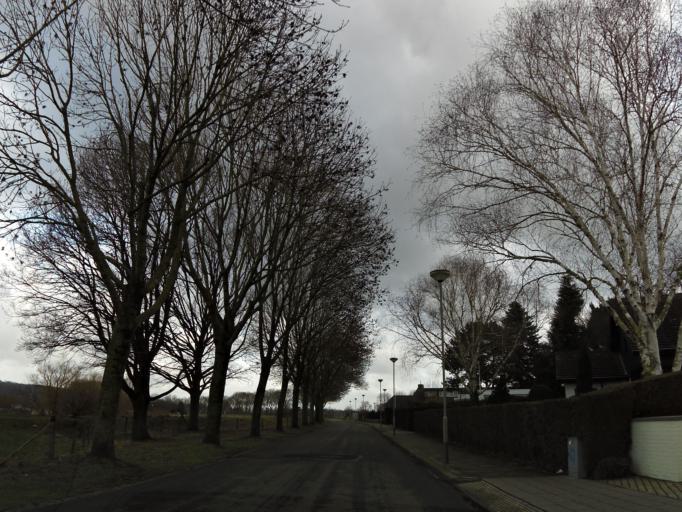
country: NL
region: Limburg
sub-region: Eijsden-Margraten
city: Eijsden
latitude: 50.7818
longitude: 5.7026
